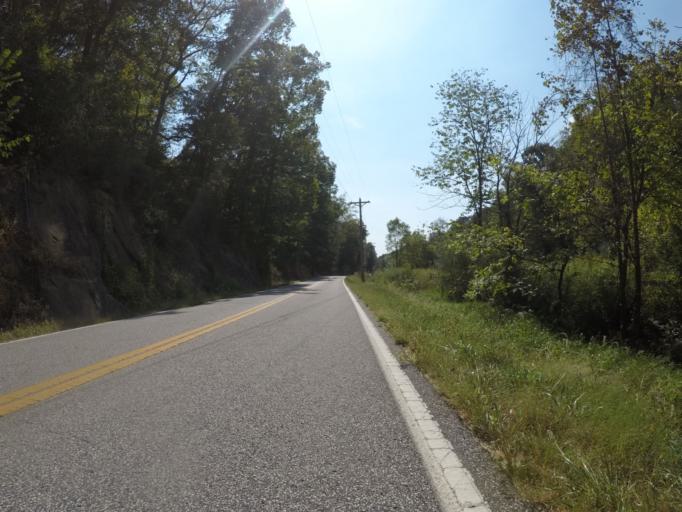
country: US
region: West Virginia
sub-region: Cabell County
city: Lesage
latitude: 38.5743
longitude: -82.4053
